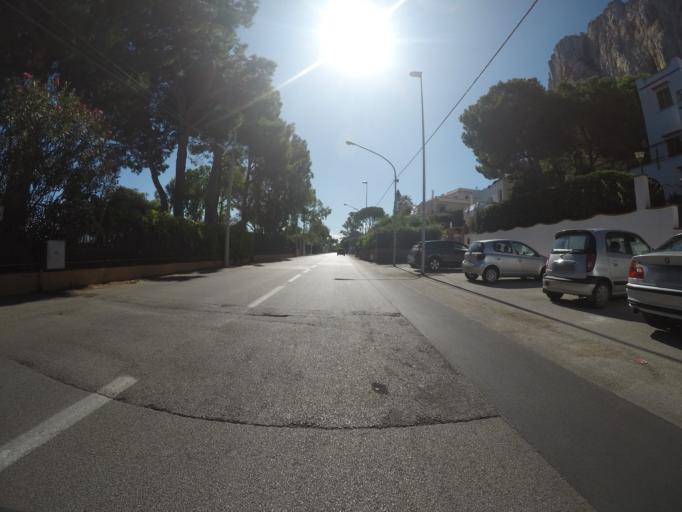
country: IT
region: Sicily
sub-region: Palermo
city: Palermo
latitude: 38.1849
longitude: 13.3625
